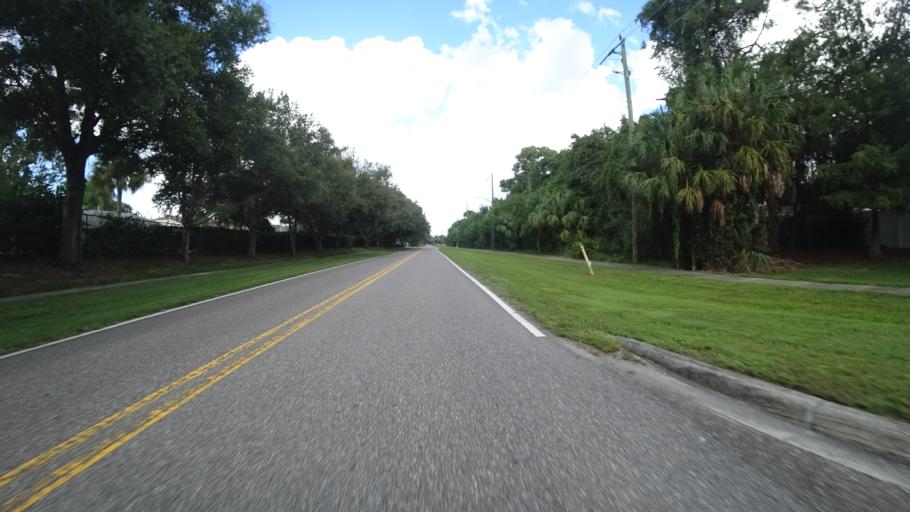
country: US
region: Florida
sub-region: Manatee County
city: Samoset
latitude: 27.4338
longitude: -82.5136
